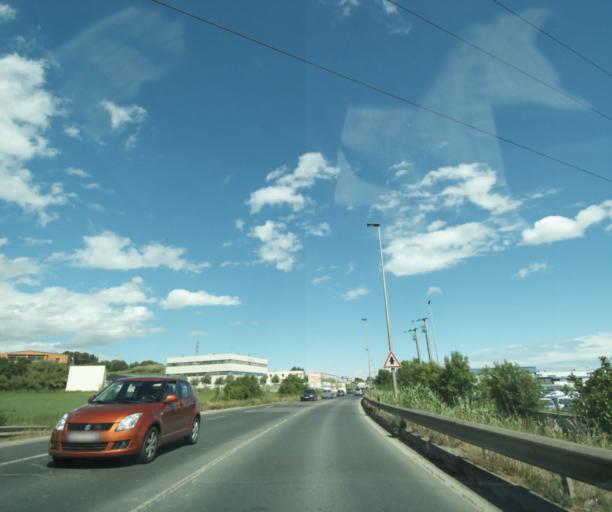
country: FR
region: Languedoc-Roussillon
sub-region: Departement de l'Herault
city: Saint-Jean-de-Vedas
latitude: 43.5752
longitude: 3.8546
